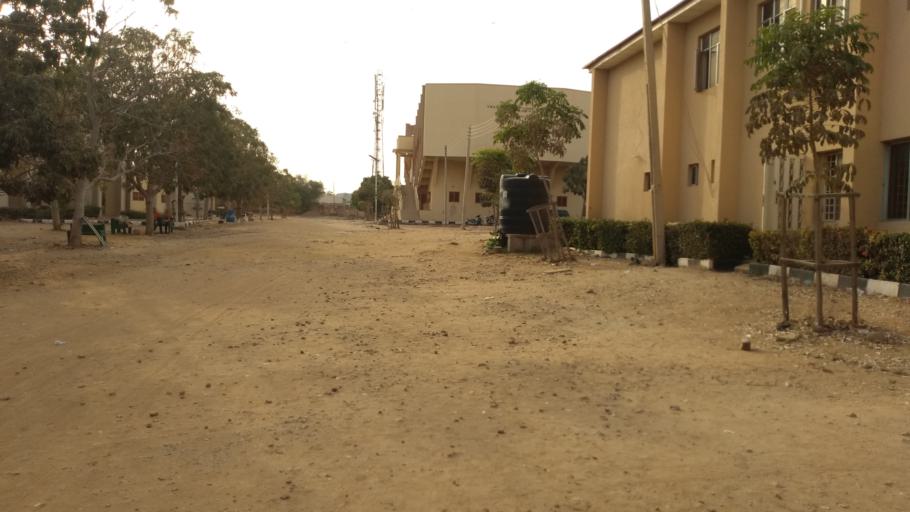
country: NG
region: Gombe
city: Gombe
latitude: 10.3057
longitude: 11.1722
